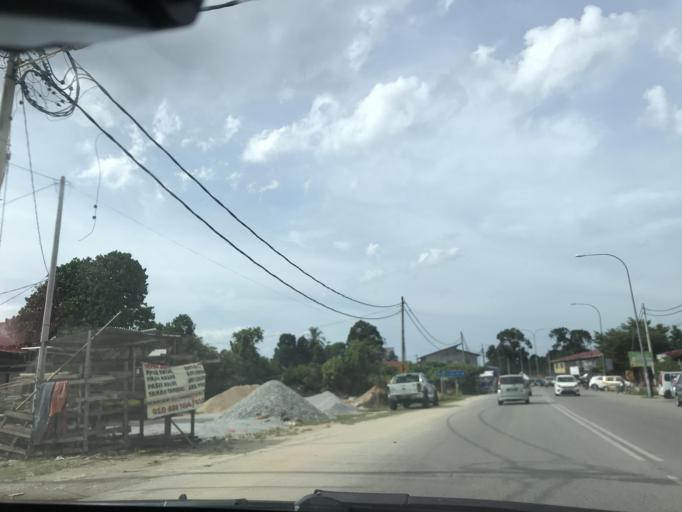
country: MY
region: Kelantan
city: Kota Bharu
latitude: 6.0894
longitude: 102.2286
